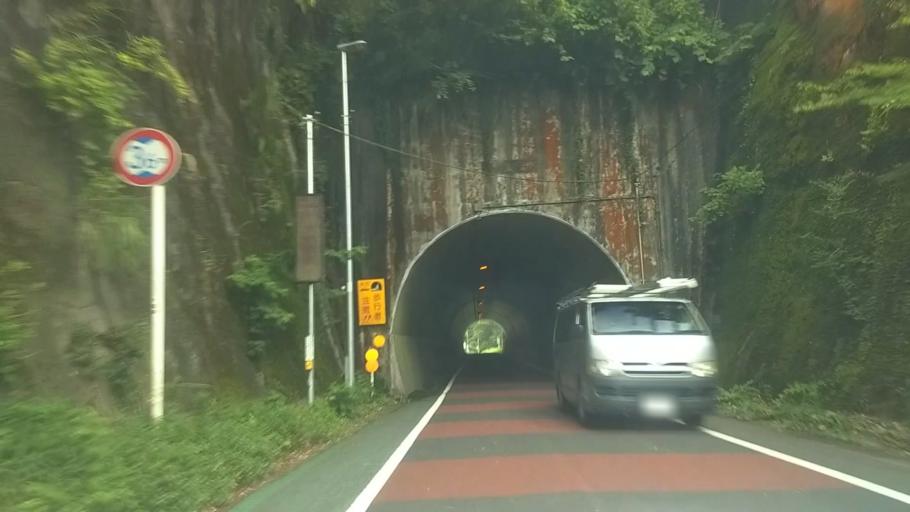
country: JP
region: Chiba
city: Kawaguchi
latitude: 35.2571
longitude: 140.0647
